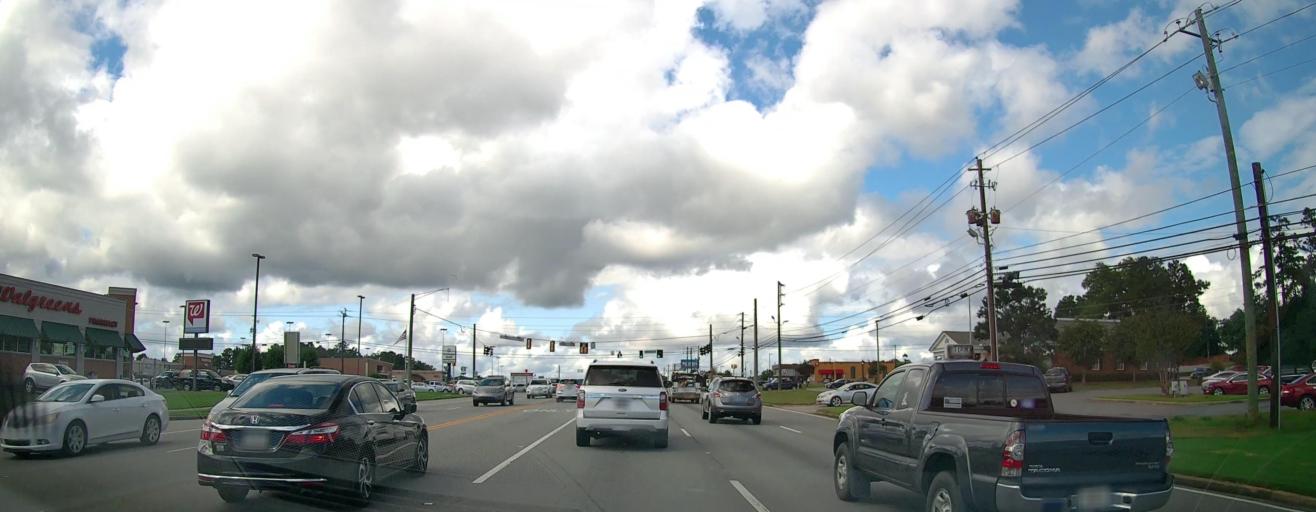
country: US
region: Georgia
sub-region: Baldwin County
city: Milledgeville
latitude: 33.1083
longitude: -83.2541
